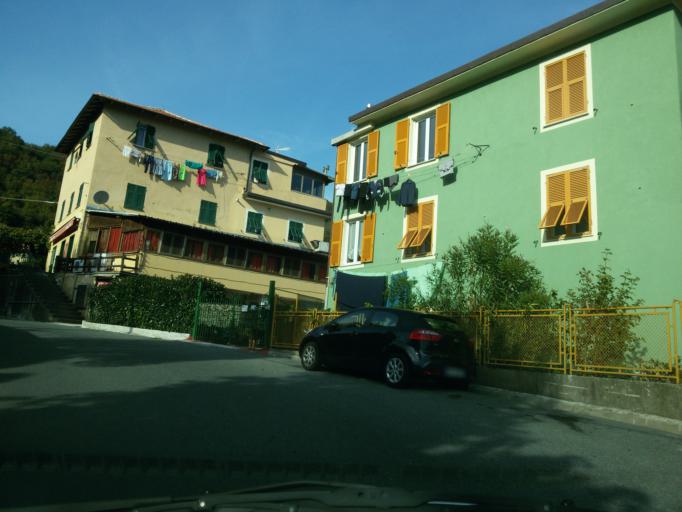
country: IT
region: Liguria
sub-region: Provincia di Genova
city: Piccarello
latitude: 44.4666
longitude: 8.9627
